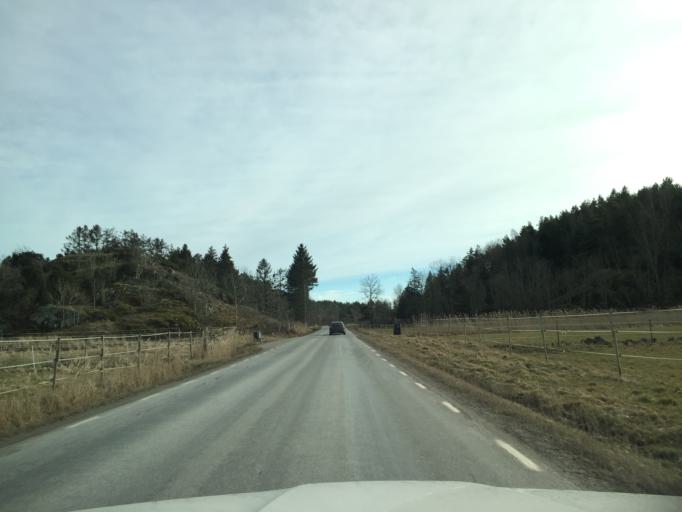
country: SE
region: Vaestra Goetaland
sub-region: Tjorns Kommun
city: Skaerhamn
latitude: 58.0342
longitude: 11.5912
